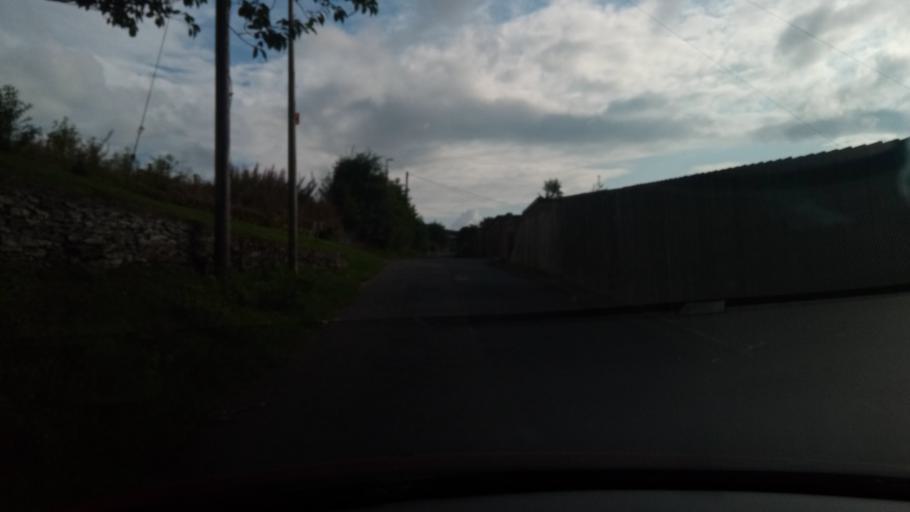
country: GB
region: Scotland
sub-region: The Scottish Borders
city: Hawick
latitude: 55.4206
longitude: -2.7801
